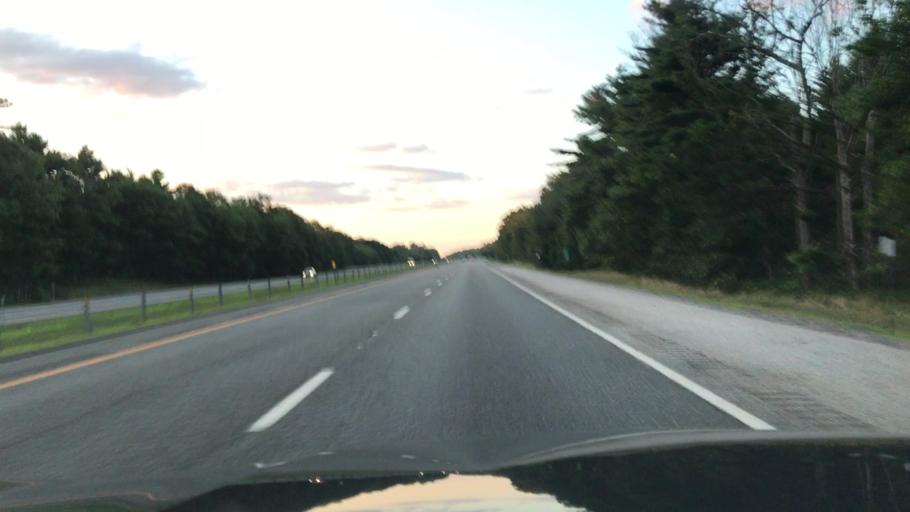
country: US
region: Rhode Island
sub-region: Kent County
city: West Greenwich
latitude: 41.5719
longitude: -71.6616
